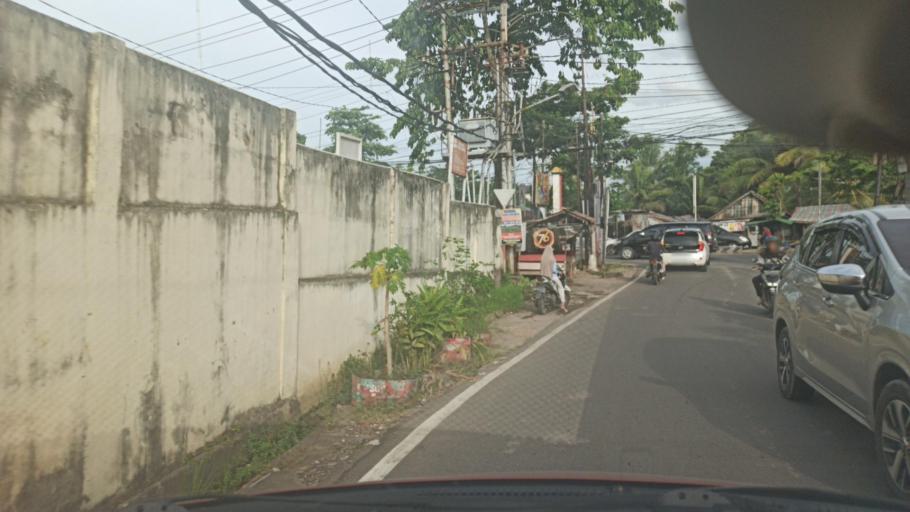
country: ID
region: South Sumatra
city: Palembang
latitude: -2.9801
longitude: 104.7238
